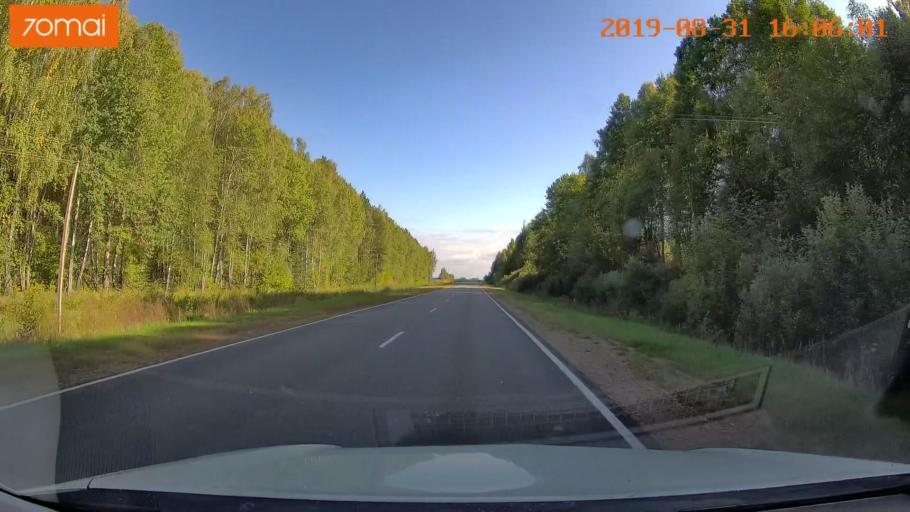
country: RU
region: Kaluga
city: Yukhnov
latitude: 54.6305
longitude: 35.3414
